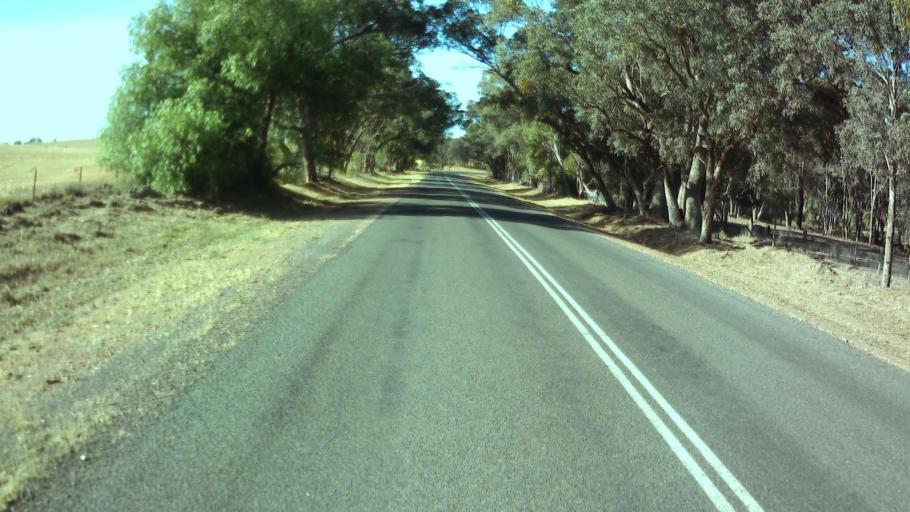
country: AU
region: New South Wales
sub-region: Weddin
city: Grenfell
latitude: -33.9961
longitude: 148.1324
